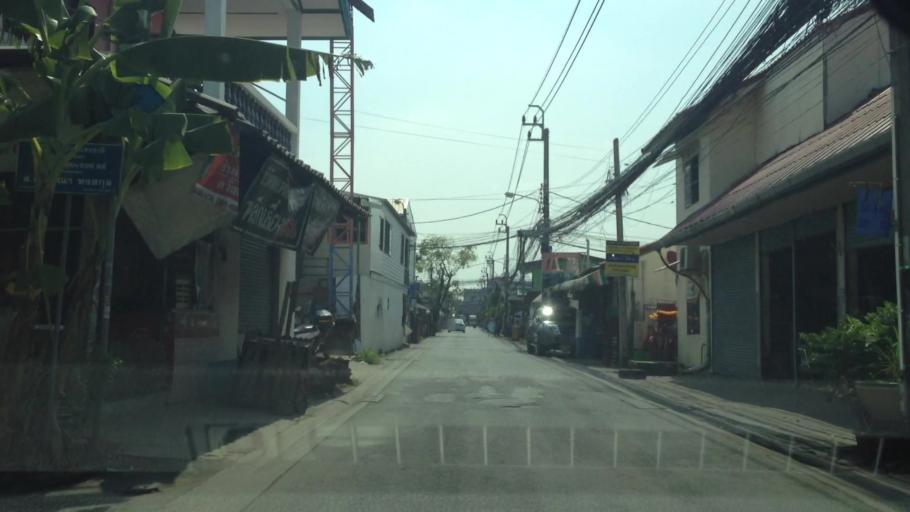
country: TH
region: Bangkok
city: Sai Mai
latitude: 13.9020
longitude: 100.6303
